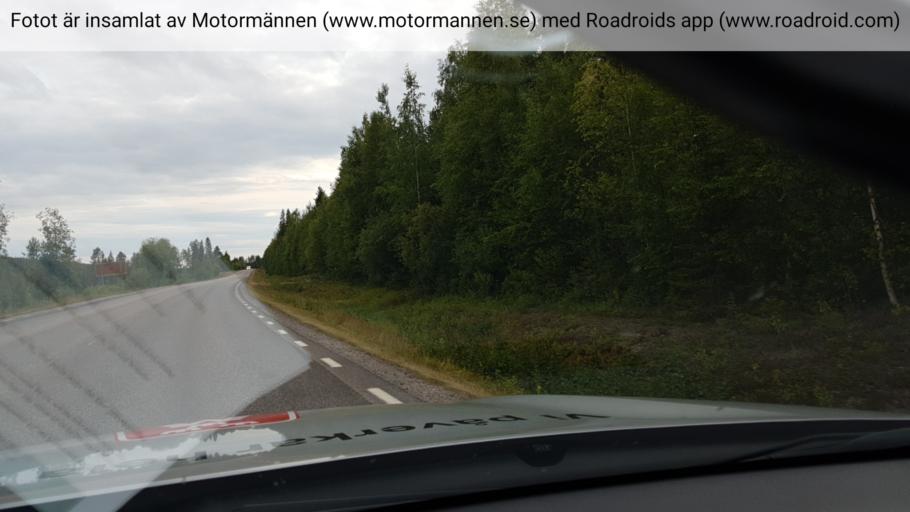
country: SE
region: Norrbotten
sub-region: Overkalix Kommun
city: OEverkalix
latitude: 66.1600
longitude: 22.8005
